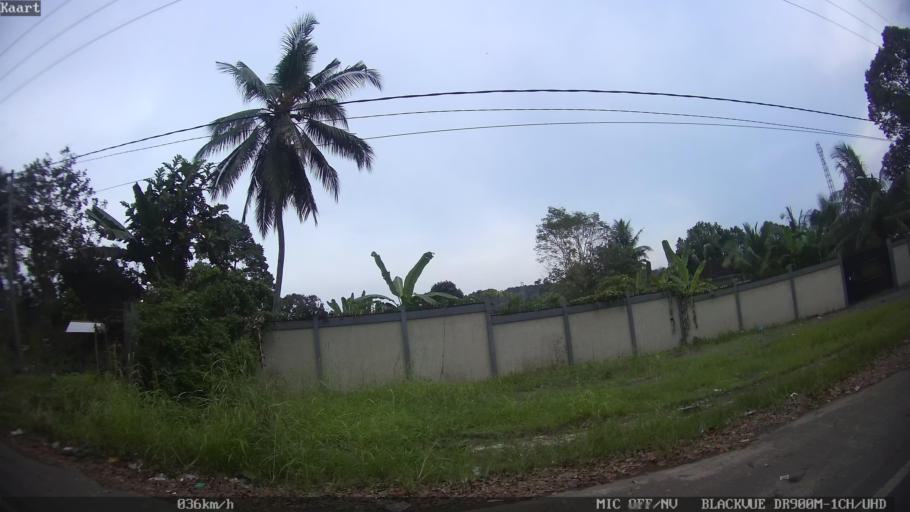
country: ID
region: Lampung
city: Bandarlampung
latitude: -5.4361
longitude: 105.2226
